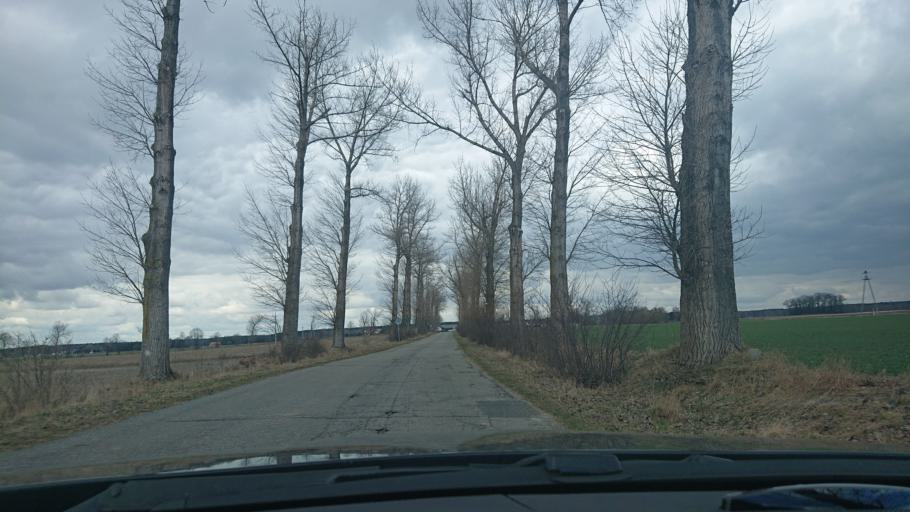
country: PL
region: Greater Poland Voivodeship
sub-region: Powiat gnieznienski
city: Niechanowo
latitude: 52.5851
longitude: 17.7008
